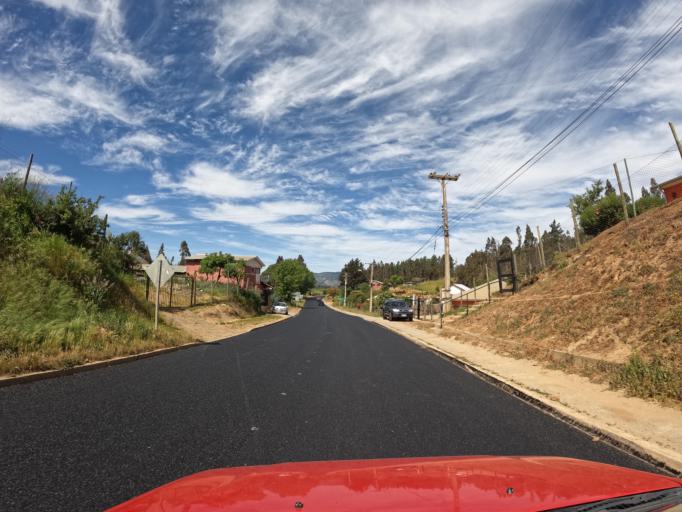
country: CL
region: Maule
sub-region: Provincia de Talca
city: Constitucion
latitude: -35.0978
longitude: -72.0088
